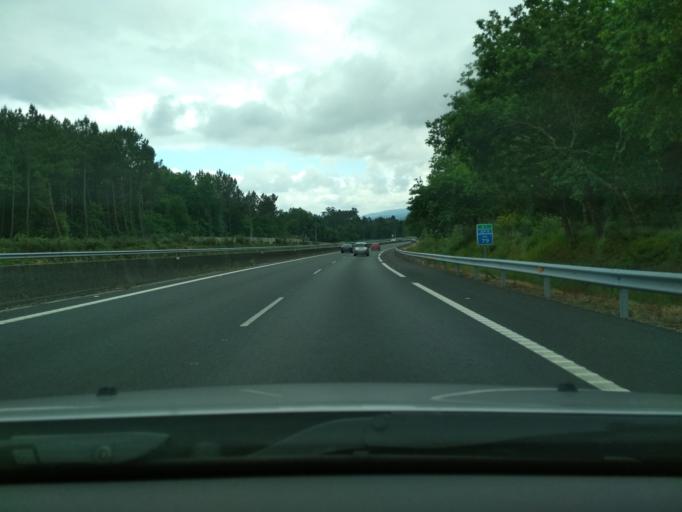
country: ES
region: Galicia
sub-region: Provincia da Coruna
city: Santiago de Compostela
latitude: 42.8231
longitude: -8.5705
